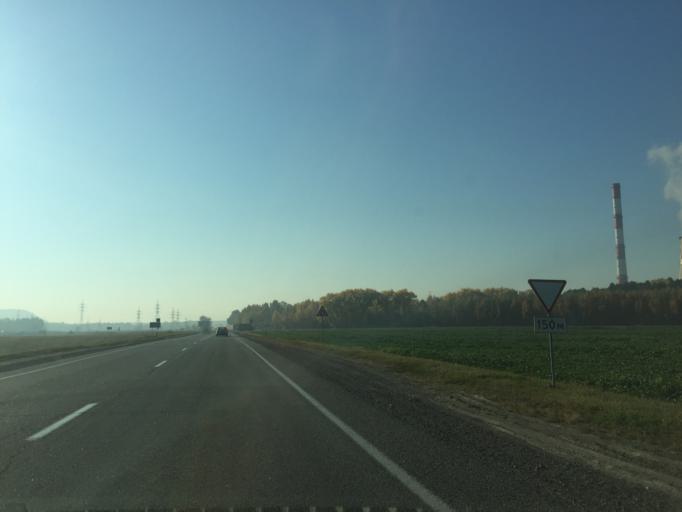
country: BY
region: Gomel
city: Kastsyukowka
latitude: 52.4560
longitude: 30.8247
